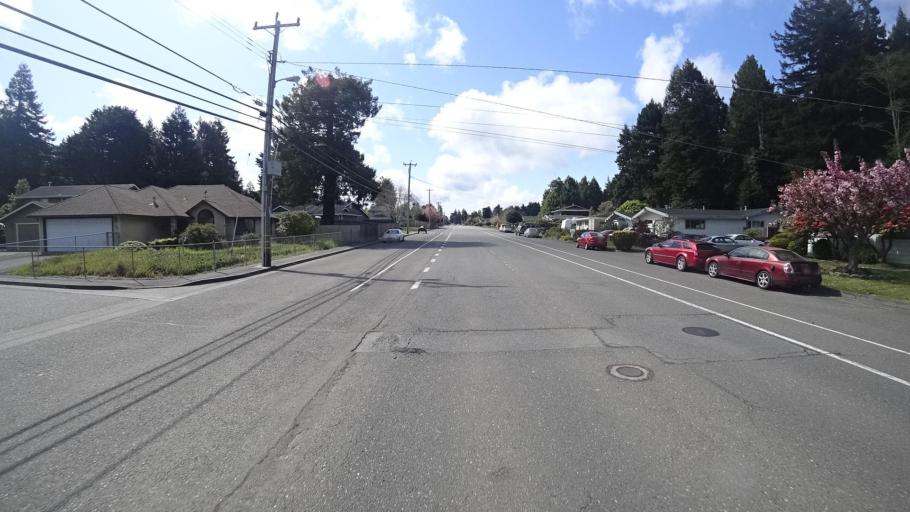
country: US
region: California
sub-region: Humboldt County
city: Pine Hills
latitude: 40.7432
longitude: -124.1474
